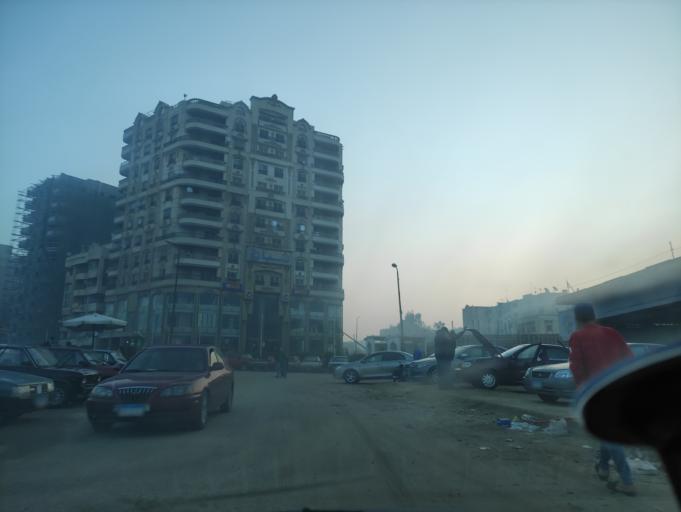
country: EG
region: Muhafazat al Qahirah
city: Cairo
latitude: 30.0480
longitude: 31.3667
